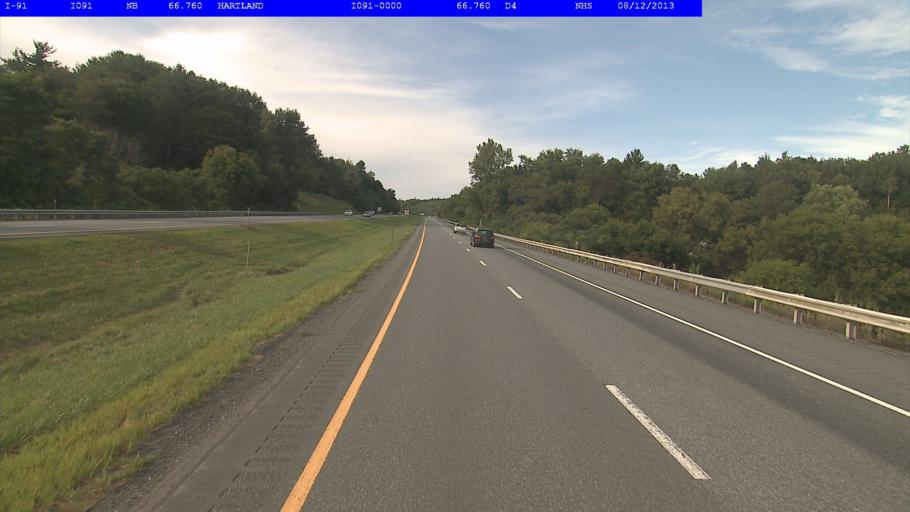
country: US
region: Vermont
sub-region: Windsor County
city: White River Junction
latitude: 43.5980
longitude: -72.3444
